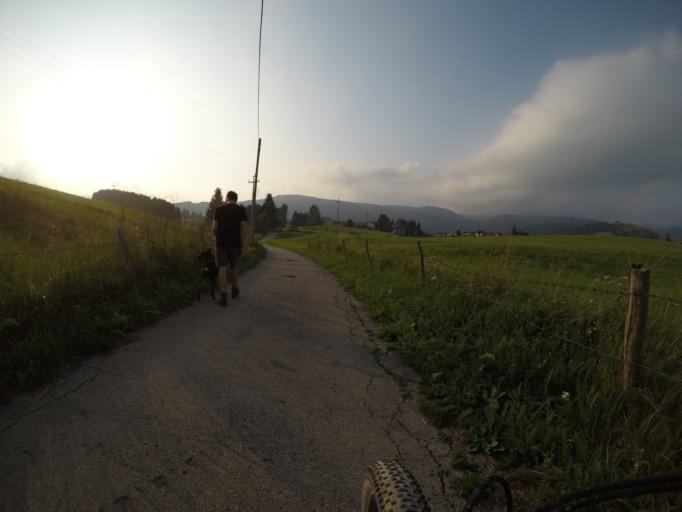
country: IT
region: Veneto
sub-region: Provincia di Vicenza
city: Asiago
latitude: 45.8807
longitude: 11.5012
